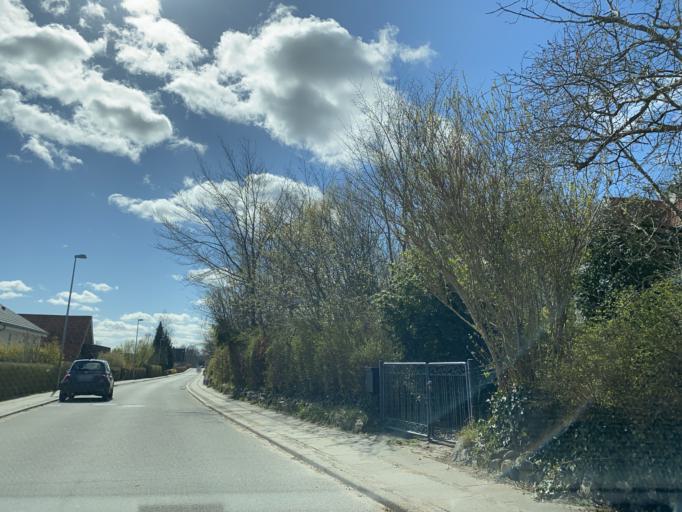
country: DK
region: Central Jutland
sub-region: Randers Kommune
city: Langa
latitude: 56.3892
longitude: 9.8915
